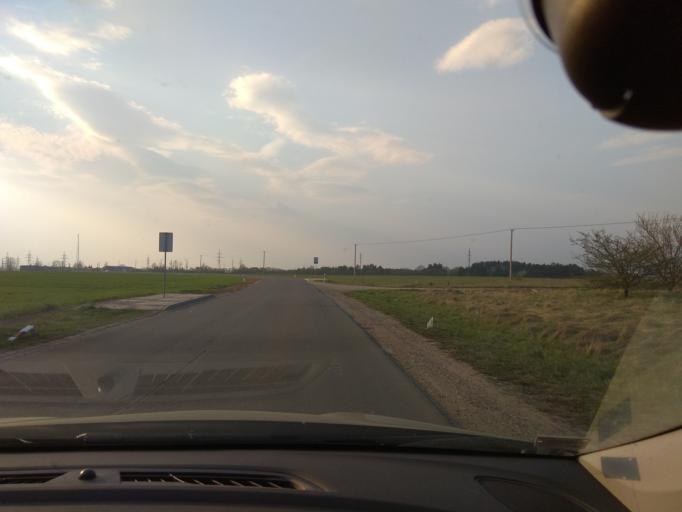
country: LT
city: Baltoji Voke
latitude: 54.6079
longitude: 25.1294
